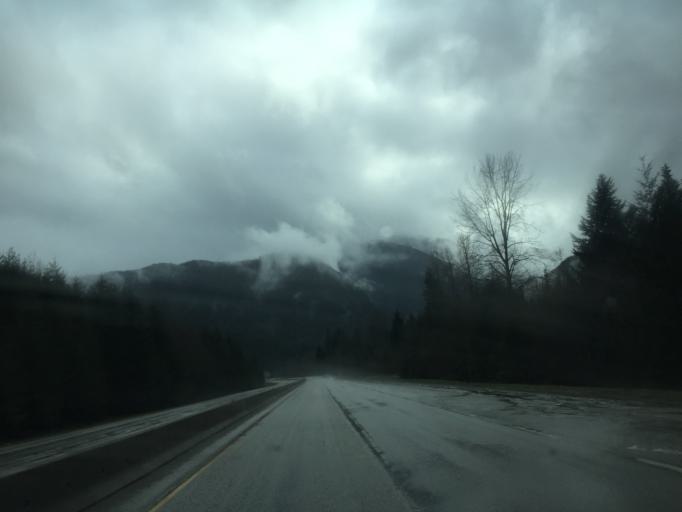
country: CA
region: British Columbia
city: Hope
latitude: 49.4729
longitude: -121.2542
